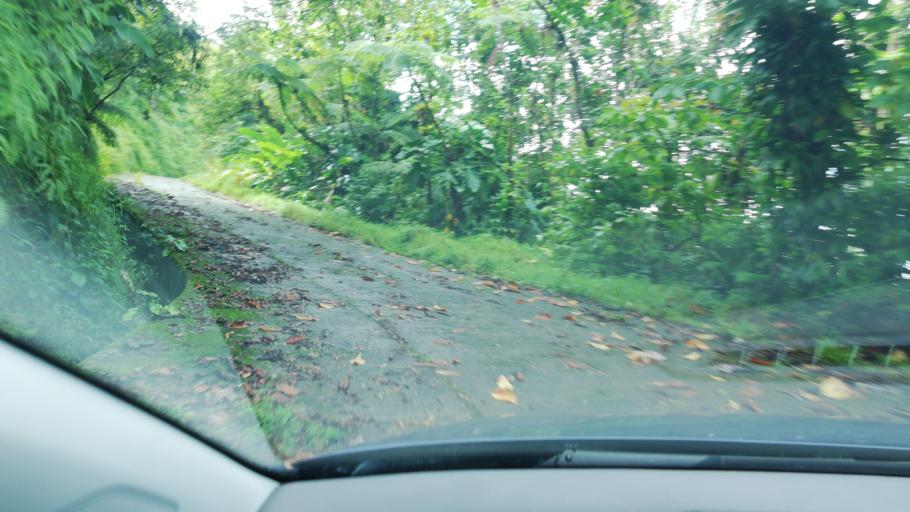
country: GP
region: Guadeloupe
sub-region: Guadeloupe
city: Pointe-Noire
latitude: 16.1890
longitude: -61.7501
